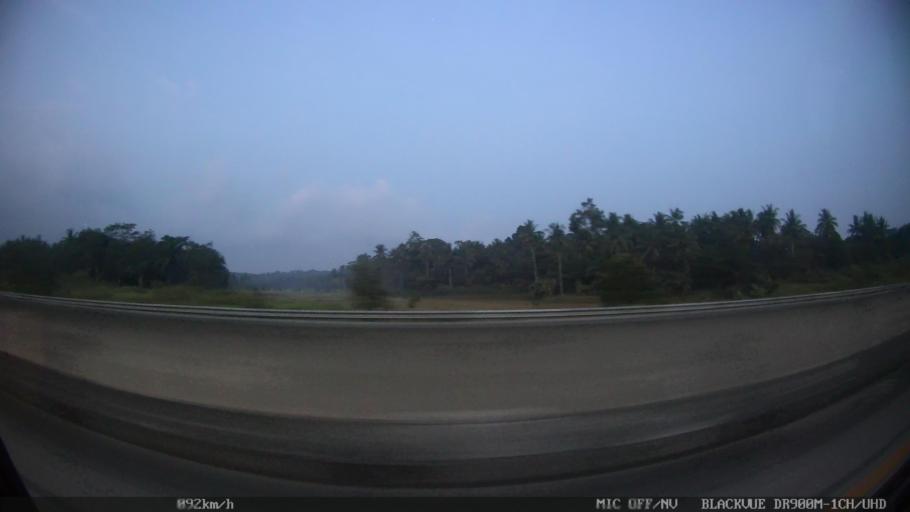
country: ID
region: Lampung
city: Sidorejo
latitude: -5.5539
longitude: 105.5256
